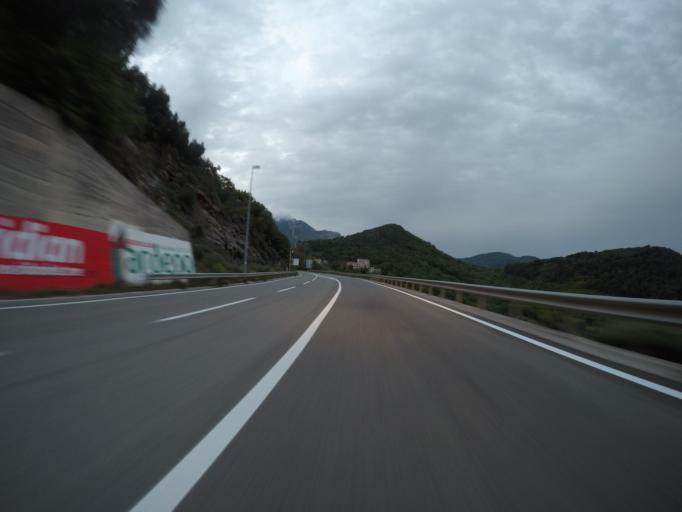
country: ME
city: Petrovac na Moru
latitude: 42.2040
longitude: 18.9517
